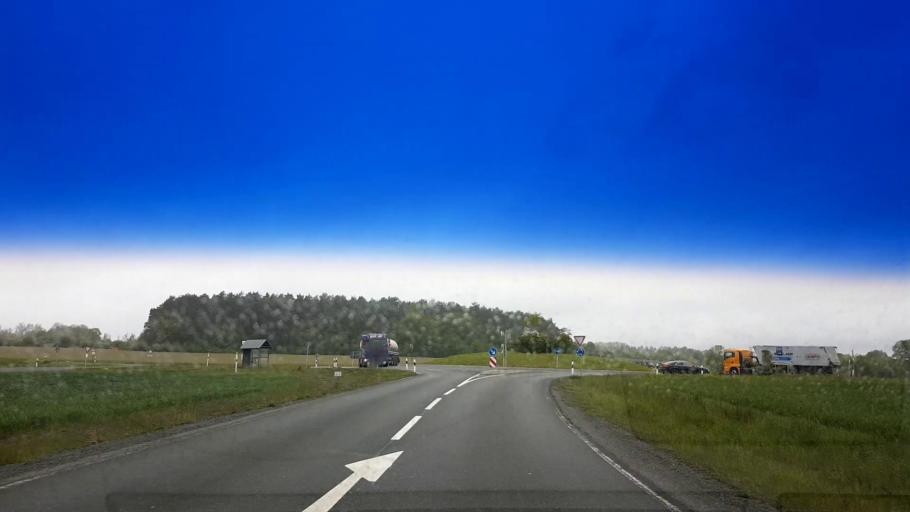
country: DE
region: Bavaria
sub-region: Upper Franconia
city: Bindlach
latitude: 50.0023
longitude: 11.6246
